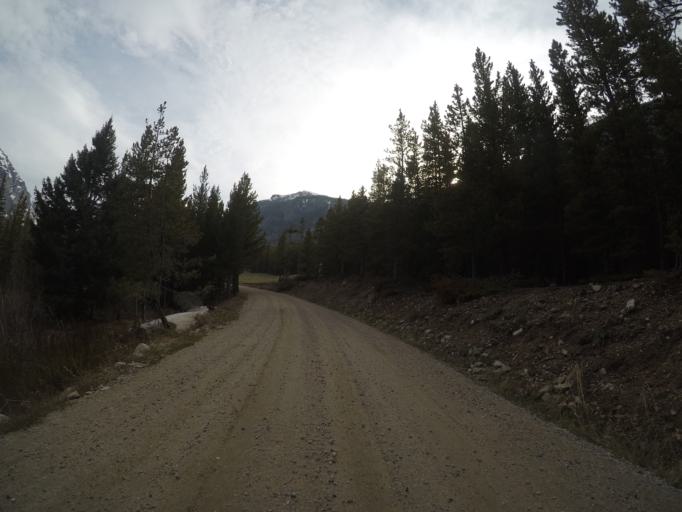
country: US
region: Montana
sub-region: Carbon County
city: Red Lodge
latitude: 45.0241
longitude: -109.4474
